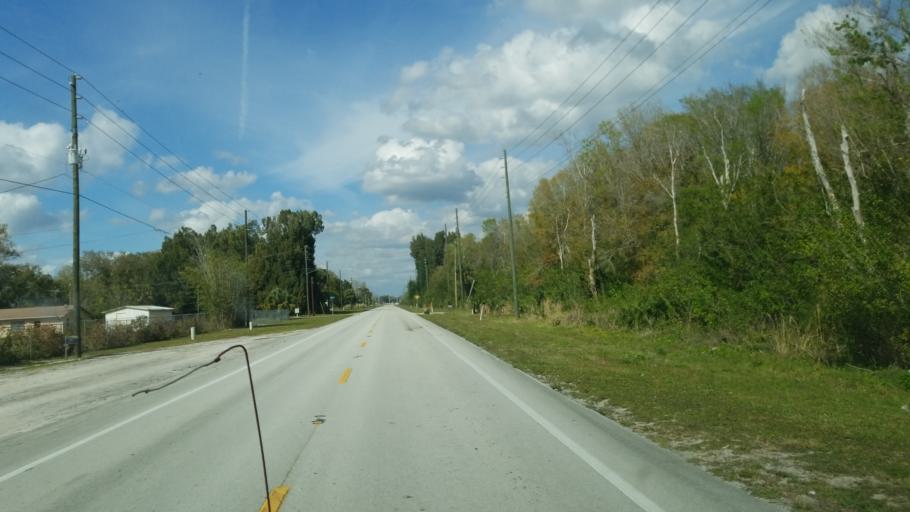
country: US
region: Florida
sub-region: Osceola County
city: Saint Cloud
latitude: 28.1349
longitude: -81.0763
